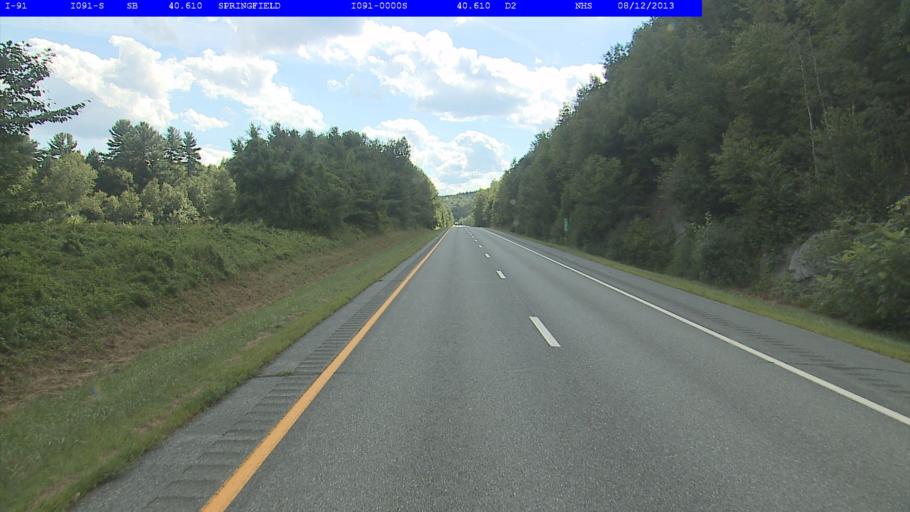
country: US
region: New Hampshire
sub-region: Sullivan County
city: Charlestown
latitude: 43.2531
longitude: -72.4421
